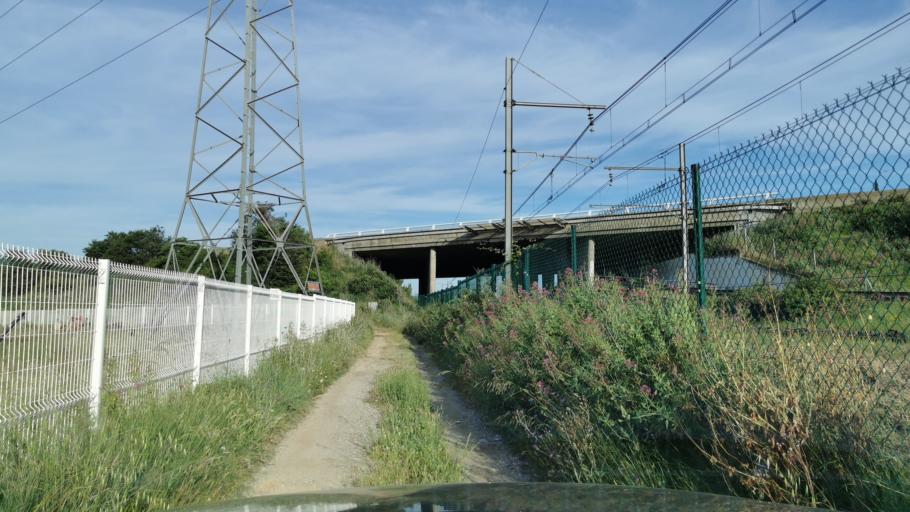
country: FR
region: Languedoc-Roussillon
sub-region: Departement de l'Aude
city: Narbonne
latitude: 43.1664
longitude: 2.9990
